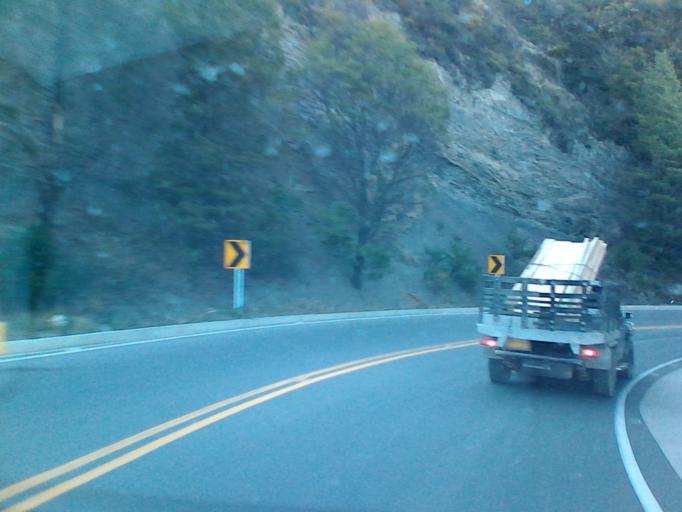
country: CO
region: Boyaca
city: Cucaita
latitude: 5.5594
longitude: -73.4314
